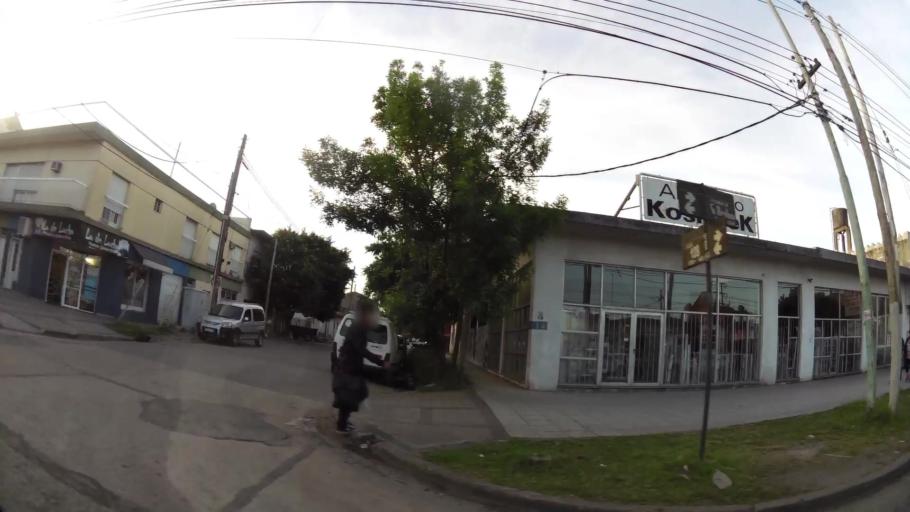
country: AR
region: Buenos Aires
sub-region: Partido de Quilmes
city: Quilmes
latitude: -34.7732
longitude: -58.2309
